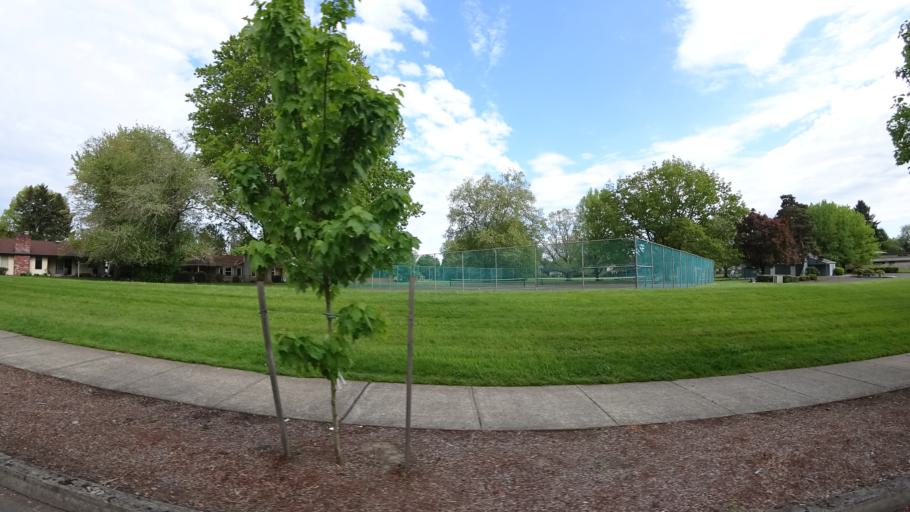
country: US
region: Oregon
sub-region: Washington County
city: Hillsboro
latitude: 45.5008
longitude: -122.9591
